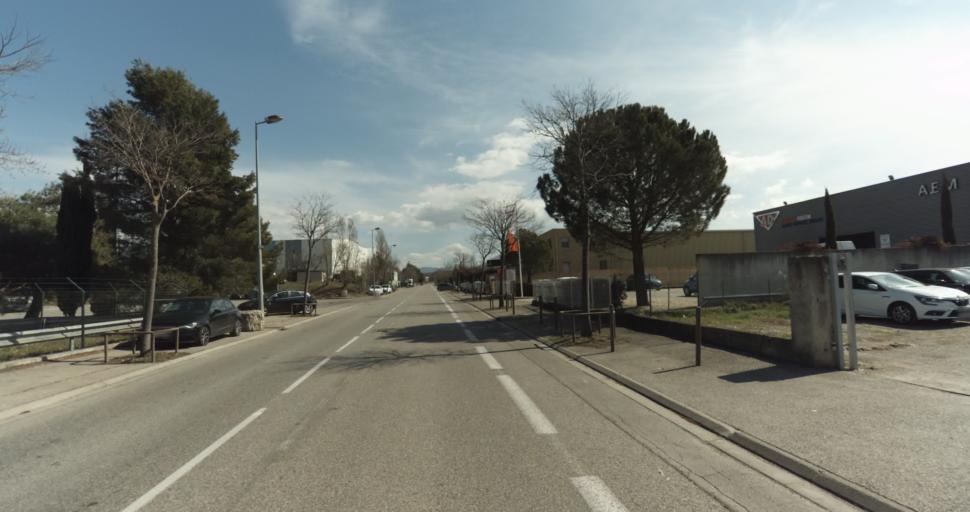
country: FR
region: Provence-Alpes-Cote d'Azur
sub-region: Departement des Bouches-du-Rhone
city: Cabries
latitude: 43.4834
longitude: 5.3761
